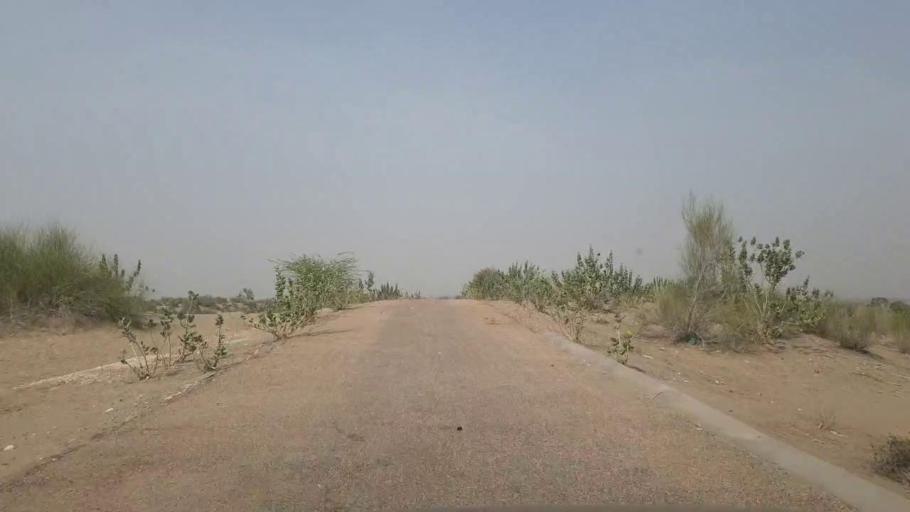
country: PK
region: Sindh
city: Chor
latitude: 25.6023
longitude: 69.9895
